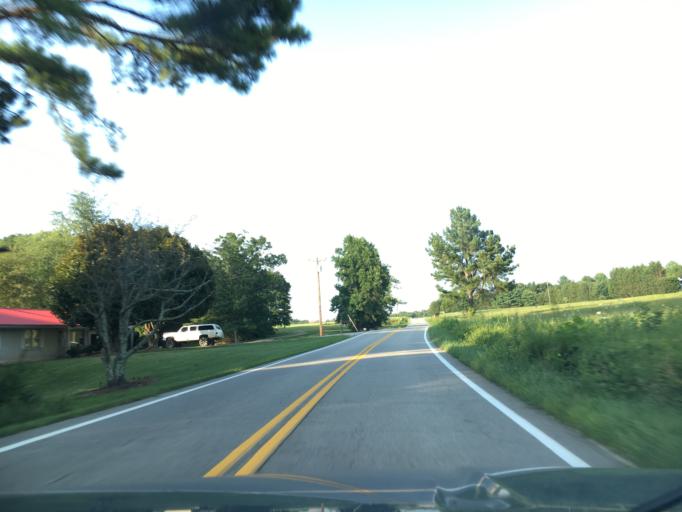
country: US
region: Virginia
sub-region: Pittsylvania County
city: Chatham
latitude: 36.8276
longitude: -79.2471
